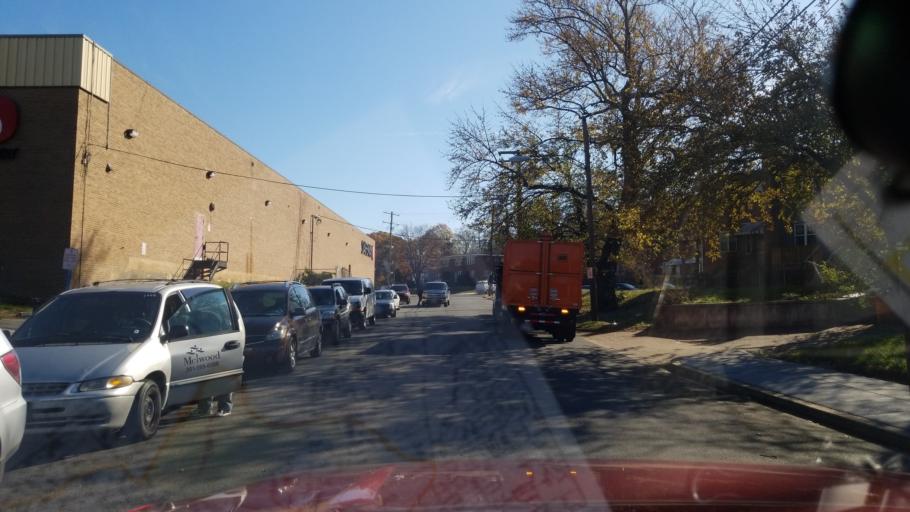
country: US
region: Maryland
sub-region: Prince George's County
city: Capitol Heights
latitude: 38.8932
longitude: -76.9486
